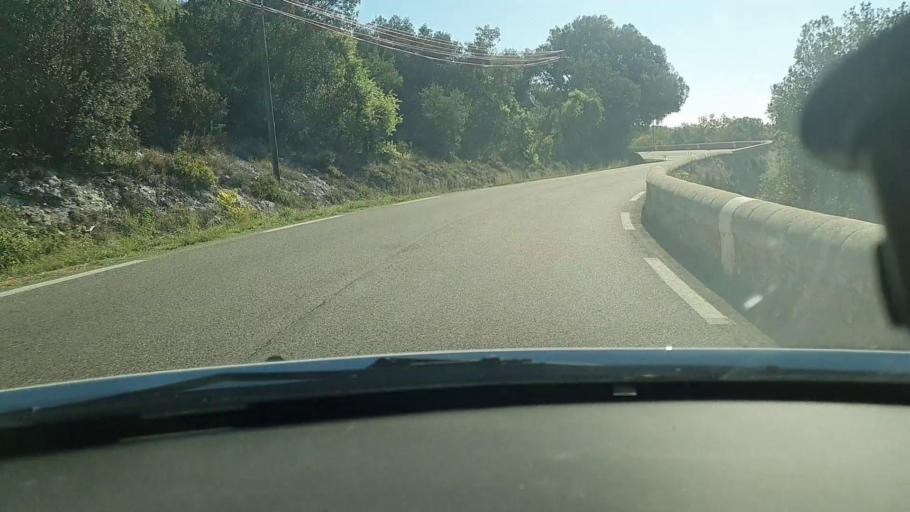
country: FR
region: Languedoc-Roussillon
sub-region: Departement du Gard
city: Saint-Julien-de-Peyrolas
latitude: 44.2974
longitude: 4.5281
